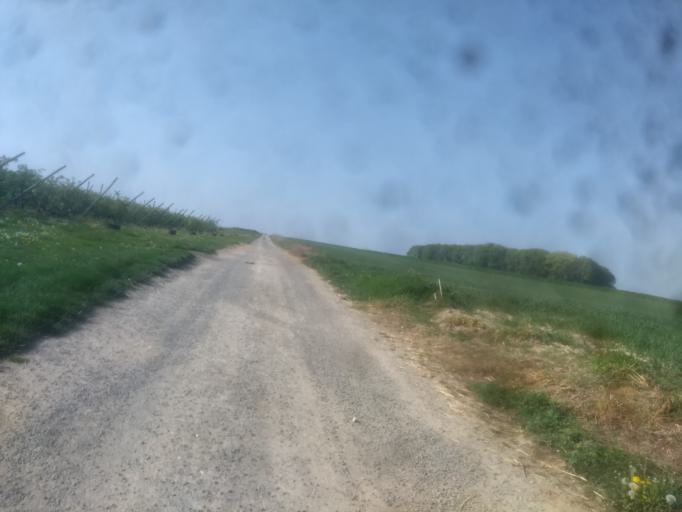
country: FR
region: Nord-Pas-de-Calais
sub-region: Departement du Pas-de-Calais
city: Beaurains
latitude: 50.2622
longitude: 2.8068
